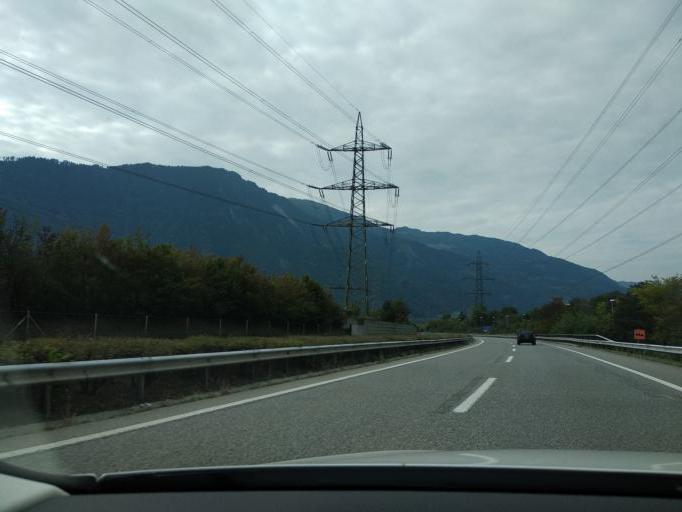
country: CH
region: Grisons
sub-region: Plessur District
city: Chur
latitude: 46.8621
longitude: 9.5092
